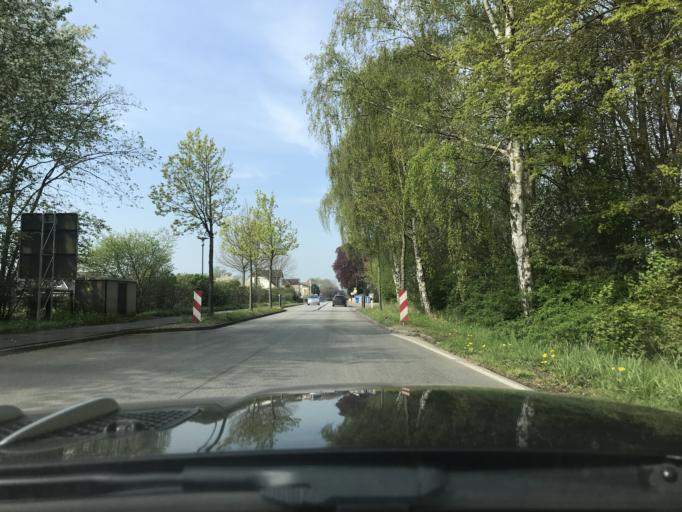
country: DE
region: Schleswig-Holstein
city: Grube
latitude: 54.1977
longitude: 11.0232
